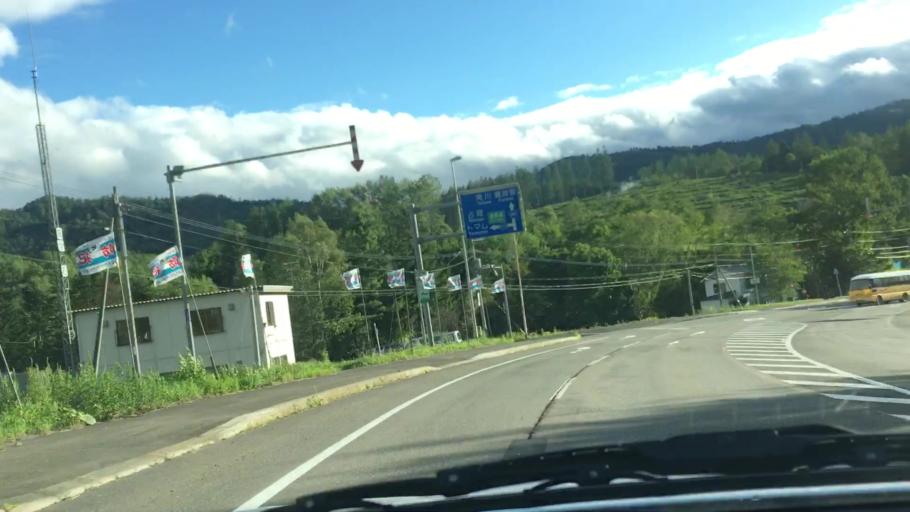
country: JP
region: Hokkaido
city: Shimo-furano
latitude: 43.1247
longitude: 142.6775
